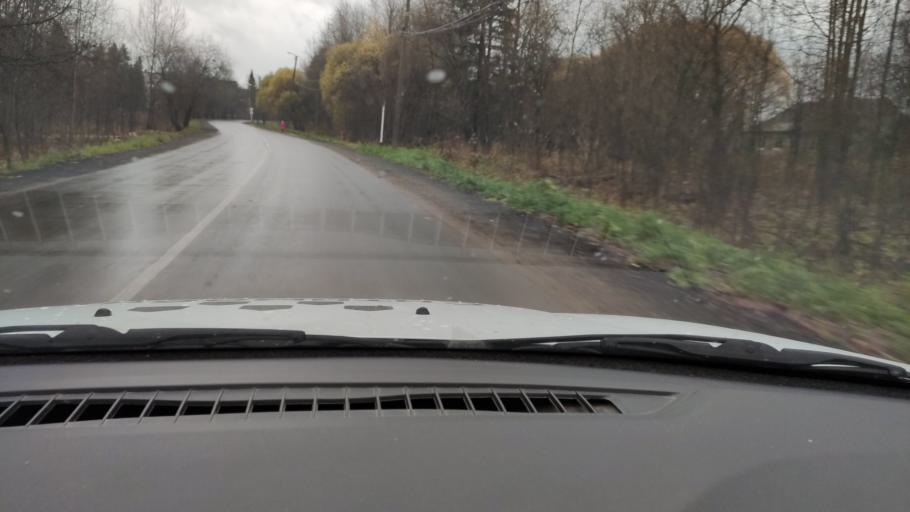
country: RU
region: Perm
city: Sylva
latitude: 58.0335
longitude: 56.7395
